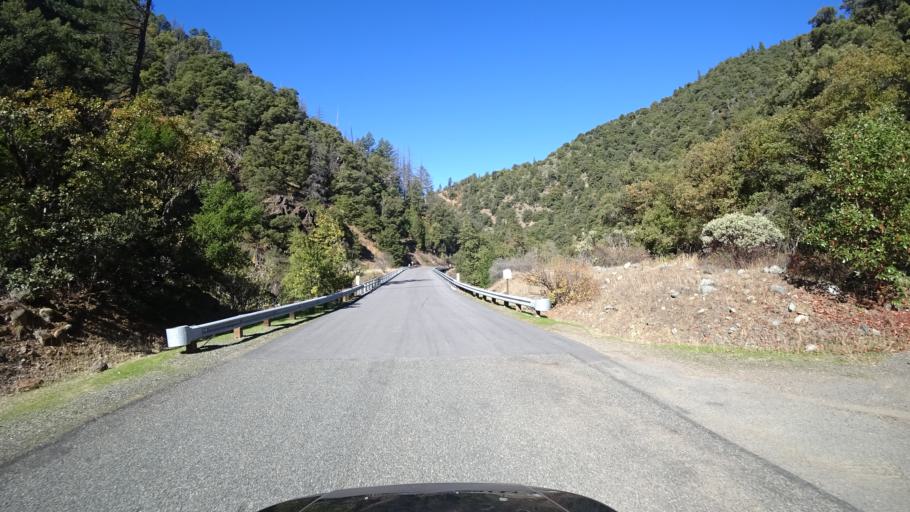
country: US
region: California
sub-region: Humboldt County
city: Willow Creek
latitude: 41.2327
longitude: -123.2597
